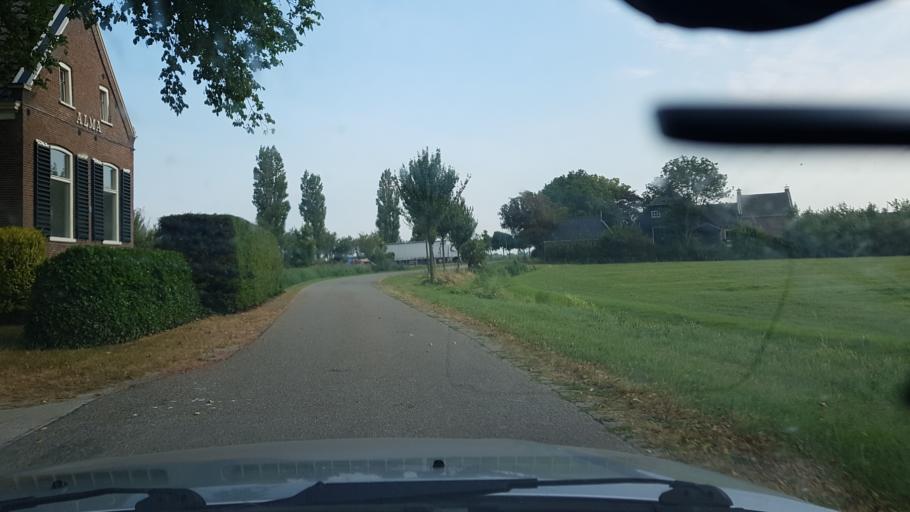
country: NL
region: Friesland
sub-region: Gemeente Dongeradeel
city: Holwerd
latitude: 53.3476
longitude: 5.8786
